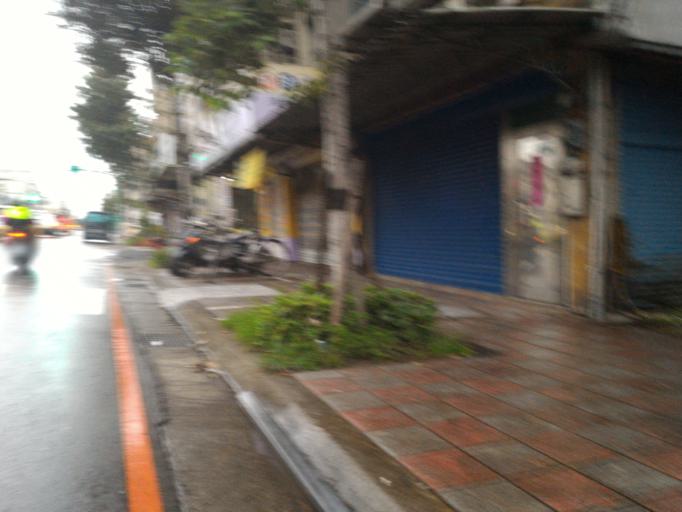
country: TW
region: Taipei
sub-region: Taipei
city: Banqiao
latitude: 24.9855
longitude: 121.4181
